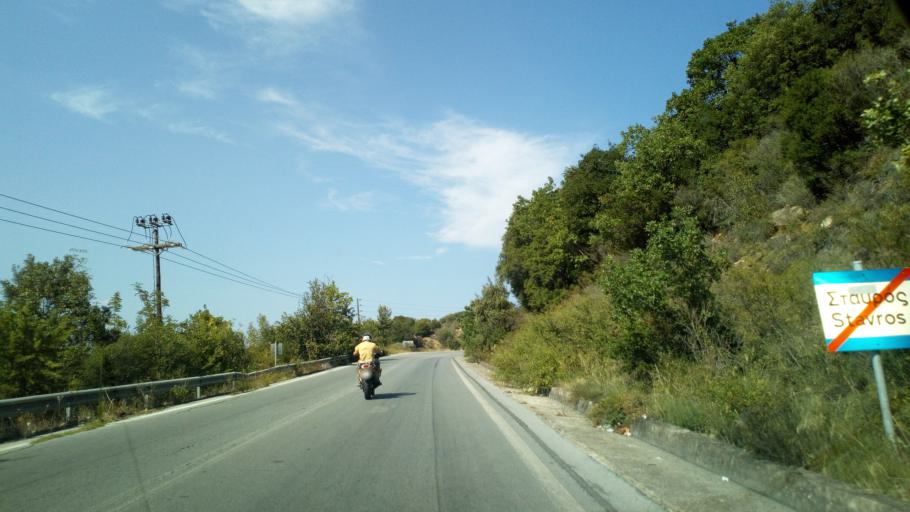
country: GR
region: Central Macedonia
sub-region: Nomos Thessalonikis
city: Stavros
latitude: 40.6561
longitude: 23.7333
